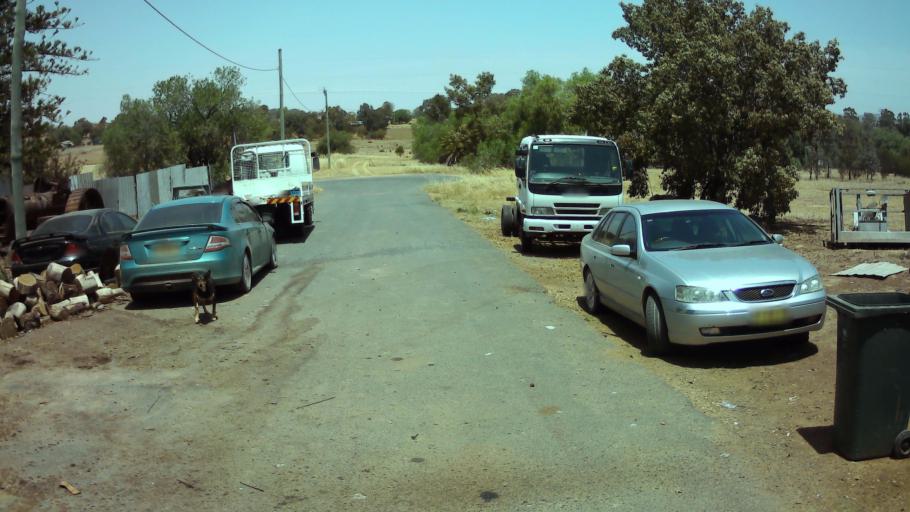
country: AU
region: New South Wales
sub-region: Weddin
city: Grenfell
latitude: -33.8973
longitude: 148.1708
